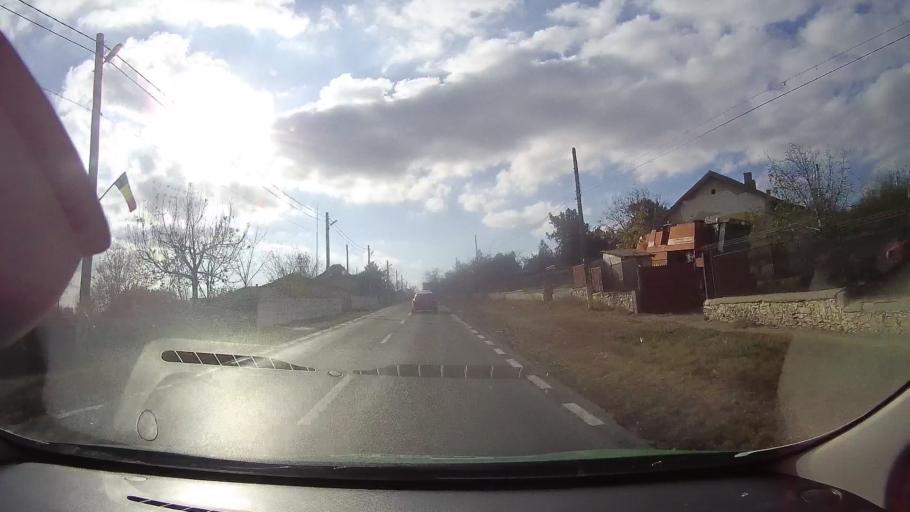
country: RO
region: Tulcea
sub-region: Comuna Topolog
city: Topolog
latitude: 44.8726
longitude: 28.3706
